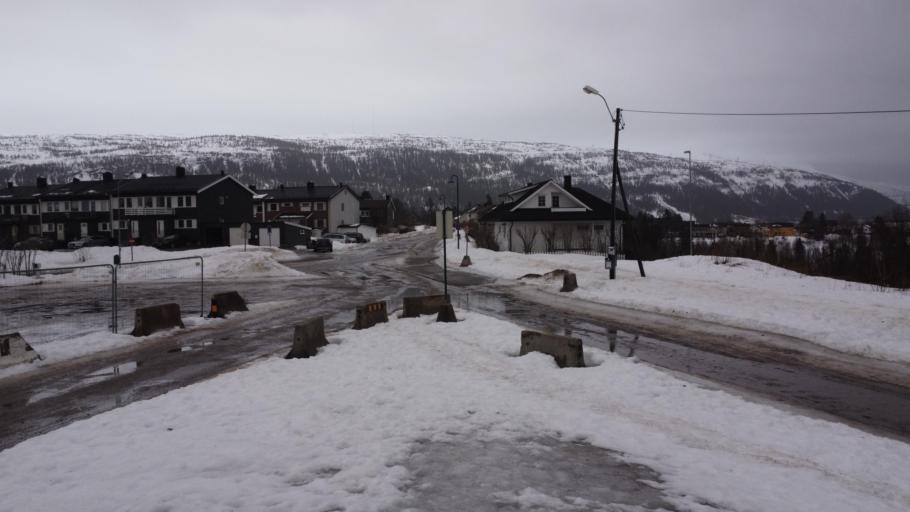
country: NO
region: Nordland
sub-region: Rana
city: Mo i Rana
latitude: 66.3188
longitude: 14.1577
